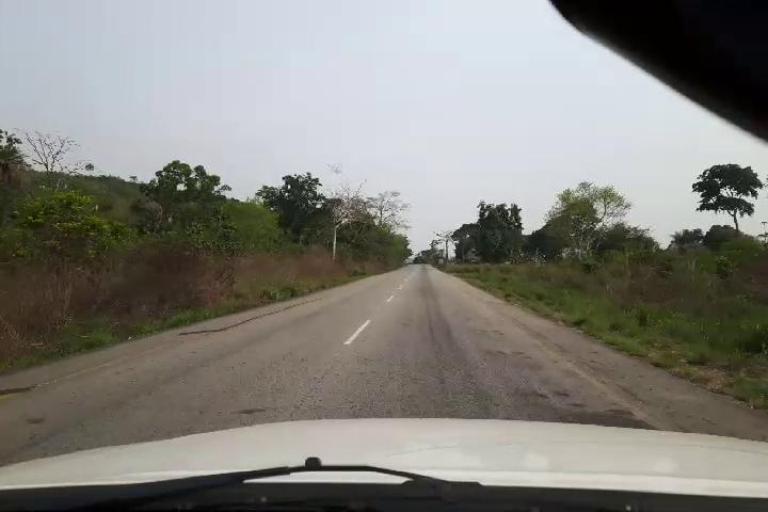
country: SL
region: Southern Province
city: Bo
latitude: 8.0081
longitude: -11.7768
